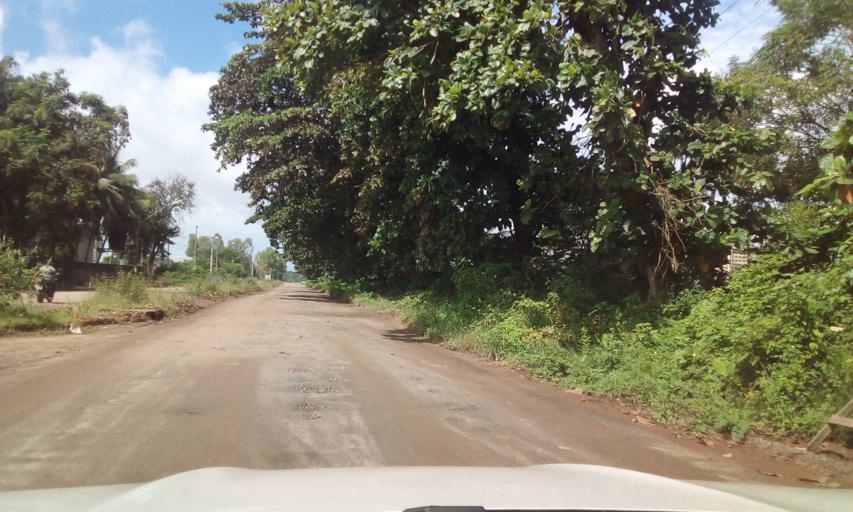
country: BR
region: Paraiba
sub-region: Conde
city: Conde
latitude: -7.1925
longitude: -34.9036
